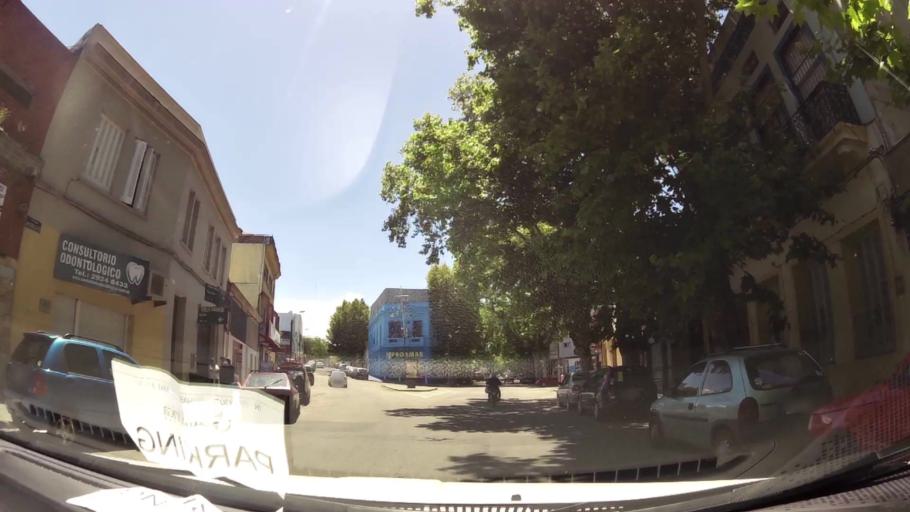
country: UY
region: Montevideo
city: Montevideo
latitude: -34.8984
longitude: -56.1867
